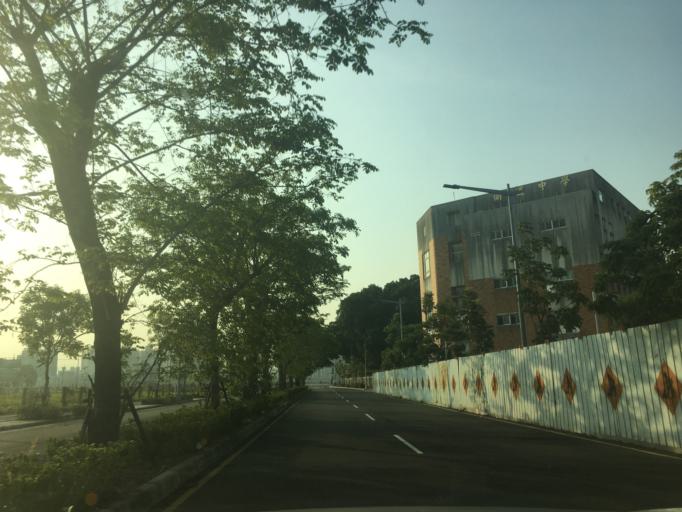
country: TW
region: Taiwan
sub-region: Taichung City
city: Taichung
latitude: 24.1855
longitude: 120.6748
